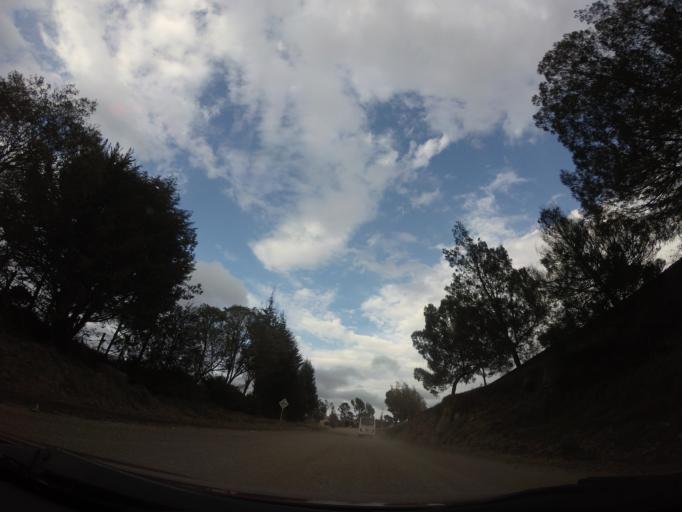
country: CO
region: Boyaca
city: Tunja
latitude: 5.5444
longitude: -73.3851
